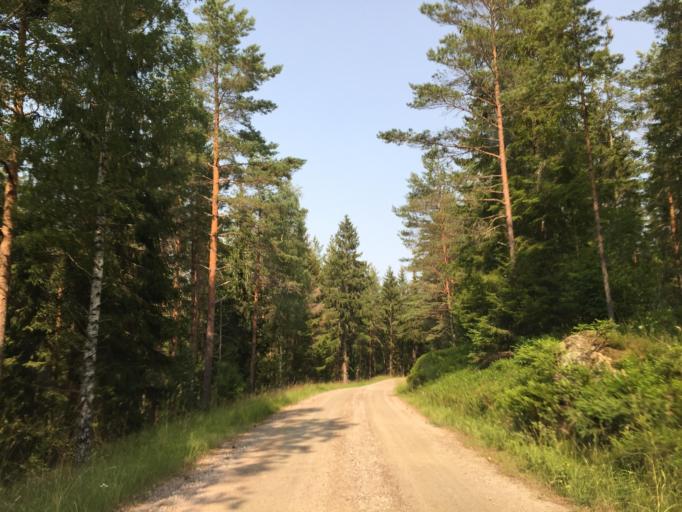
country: SE
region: Vaestra Goetaland
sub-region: Lilla Edets Kommun
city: Lilla Edet
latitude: 58.2536
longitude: 12.0918
